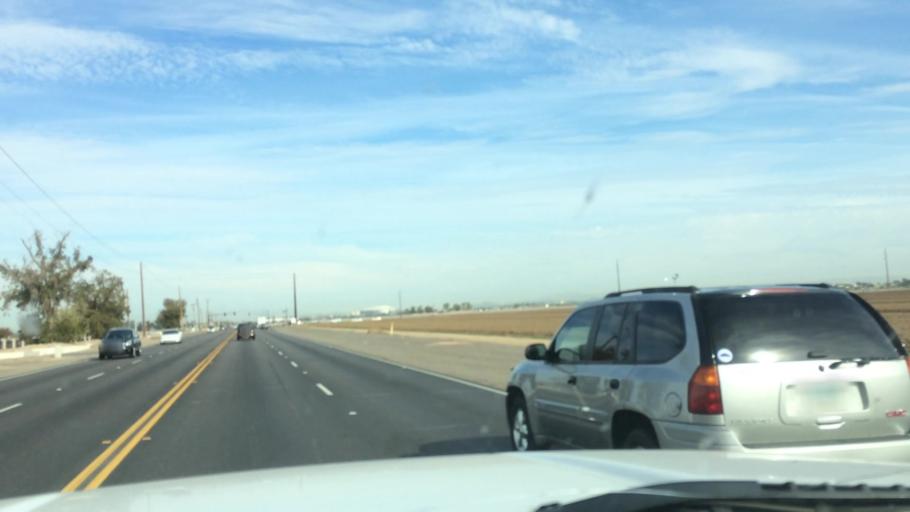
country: US
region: Arizona
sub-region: Maricopa County
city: Tolleson
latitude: 33.4760
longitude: -112.2725
